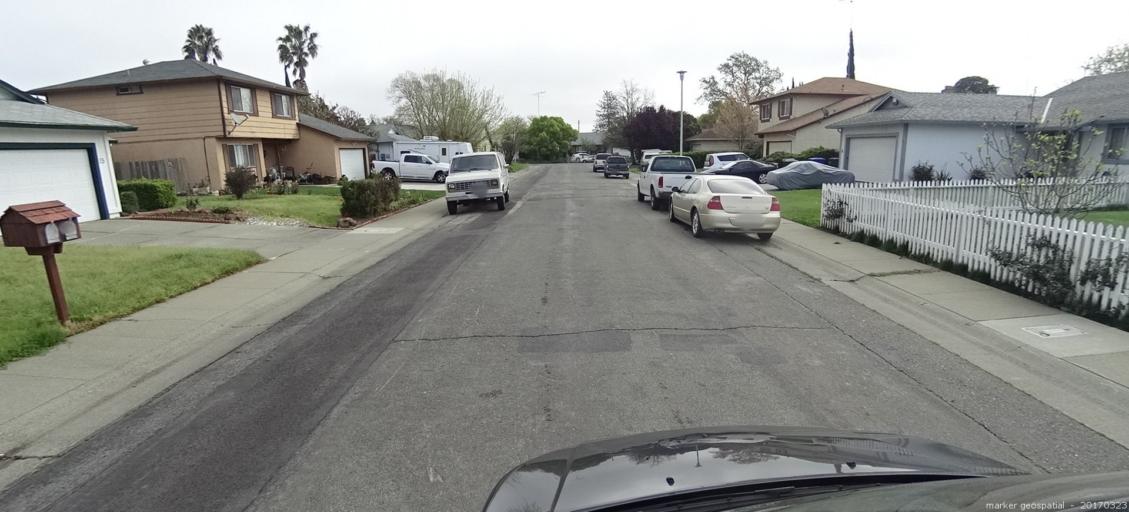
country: US
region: California
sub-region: Sacramento County
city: Florin
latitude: 38.5116
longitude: -121.4246
